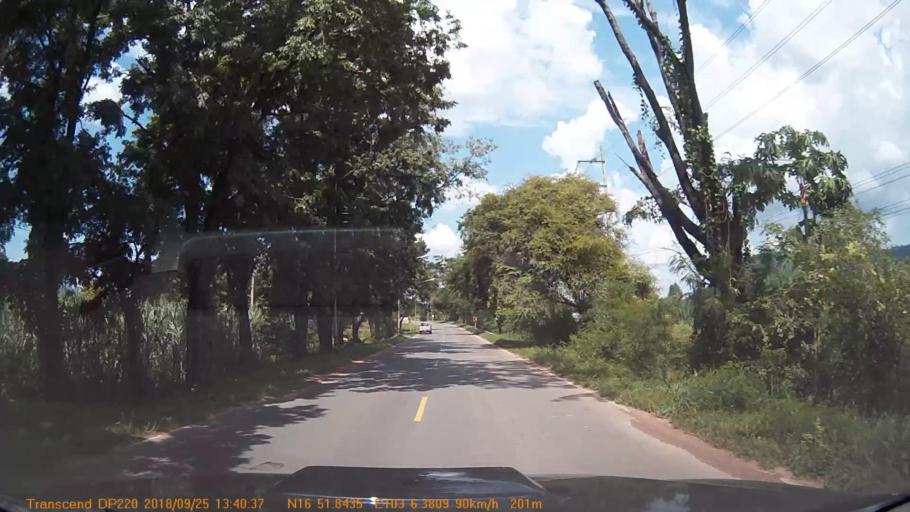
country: TH
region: Changwat Udon Thani
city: Si That
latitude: 16.8640
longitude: 103.1063
